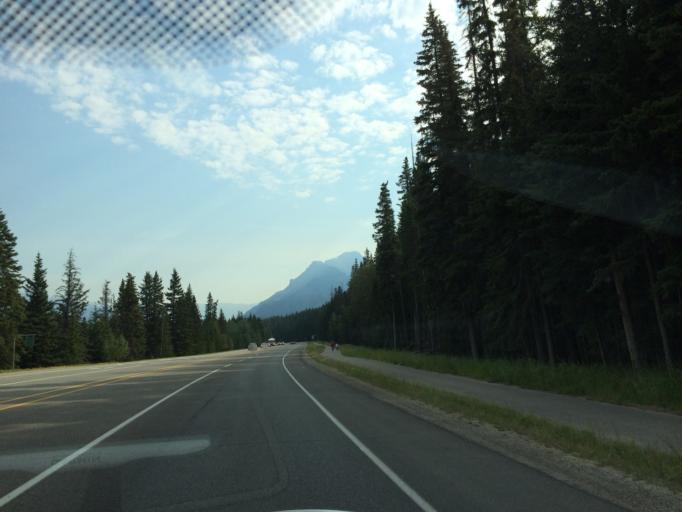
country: CA
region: Alberta
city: Banff
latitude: 51.1917
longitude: -115.5471
